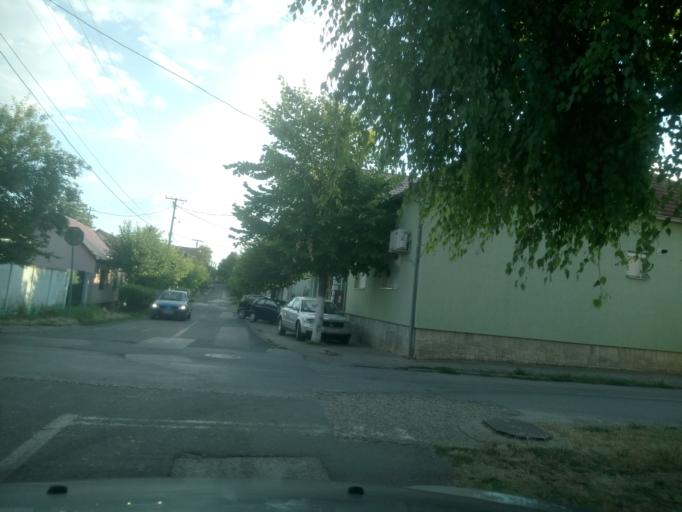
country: RS
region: Autonomna Pokrajina Vojvodina
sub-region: Sremski Okrug
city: Ingija
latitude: 45.0588
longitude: 20.0819
